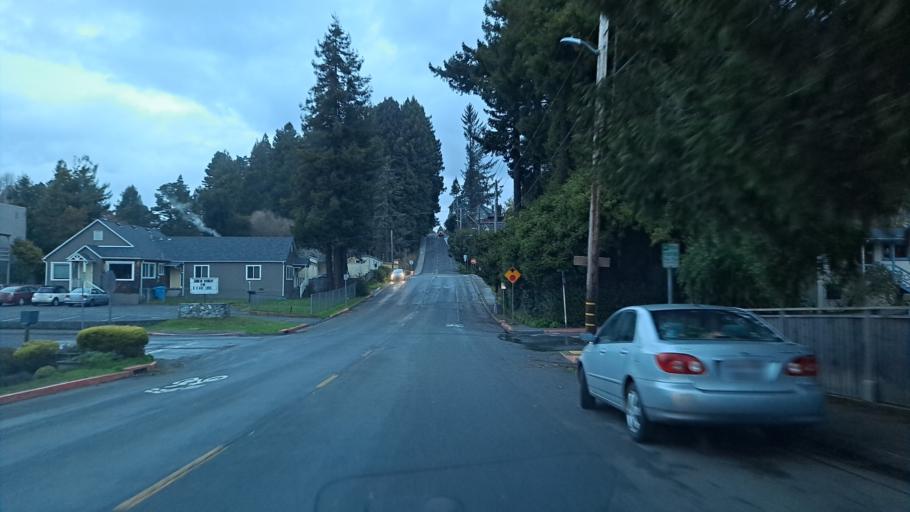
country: US
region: California
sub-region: Humboldt County
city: Arcata
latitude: 40.8702
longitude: -124.0774
